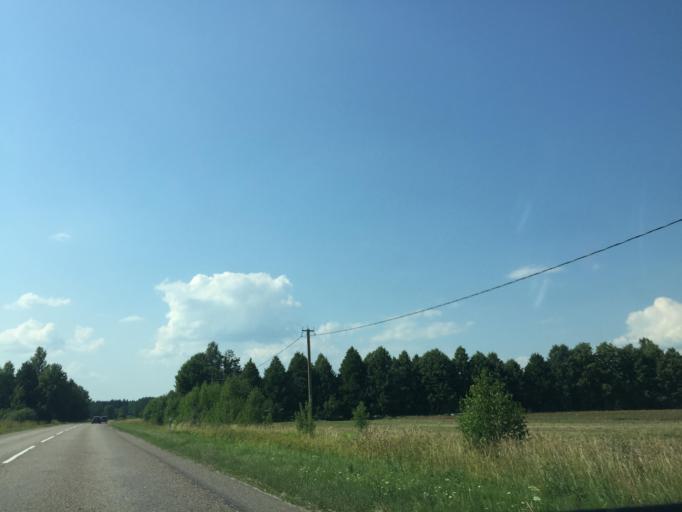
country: LV
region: Limbazu Rajons
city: Limbazi
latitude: 57.4849
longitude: 24.8633
